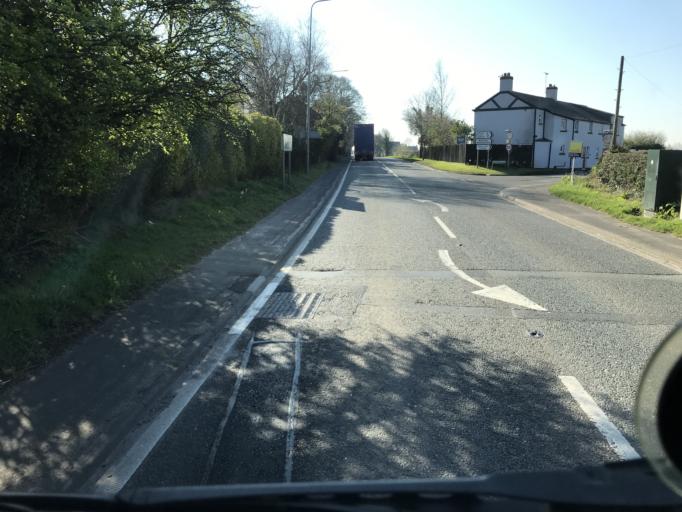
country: GB
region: England
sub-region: Cheshire West and Chester
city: Waverton
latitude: 53.1694
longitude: -2.8212
